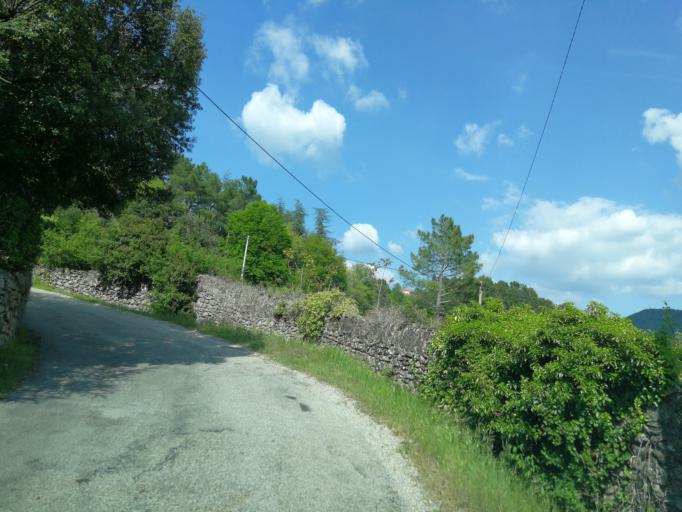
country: FR
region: Rhone-Alpes
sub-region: Departement de l'Ardeche
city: Saint-Sauveur-de-Montagut
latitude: 44.8076
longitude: 4.6177
